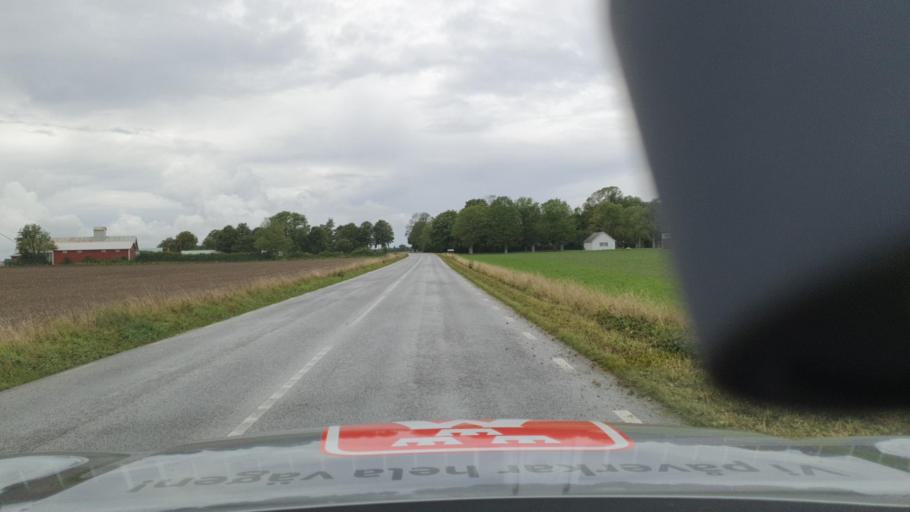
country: SE
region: Gotland
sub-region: Gotland
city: Visby
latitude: 57.5064
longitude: 18.4162
